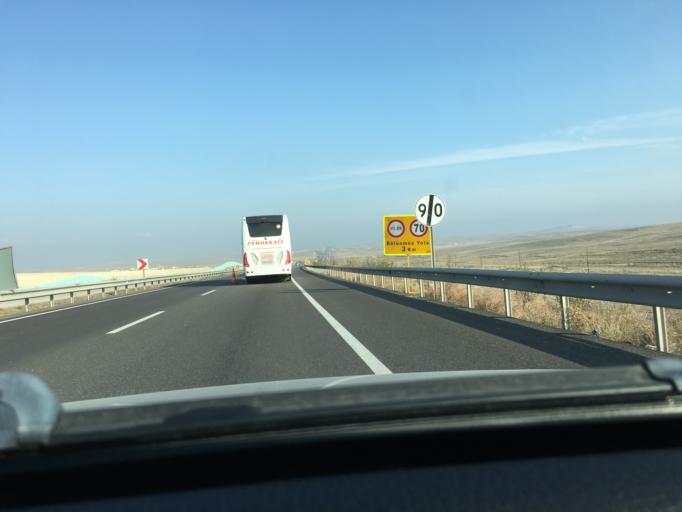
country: TR
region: Eskisehir
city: Gunyuzu
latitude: 39.5741
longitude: 31.8446
